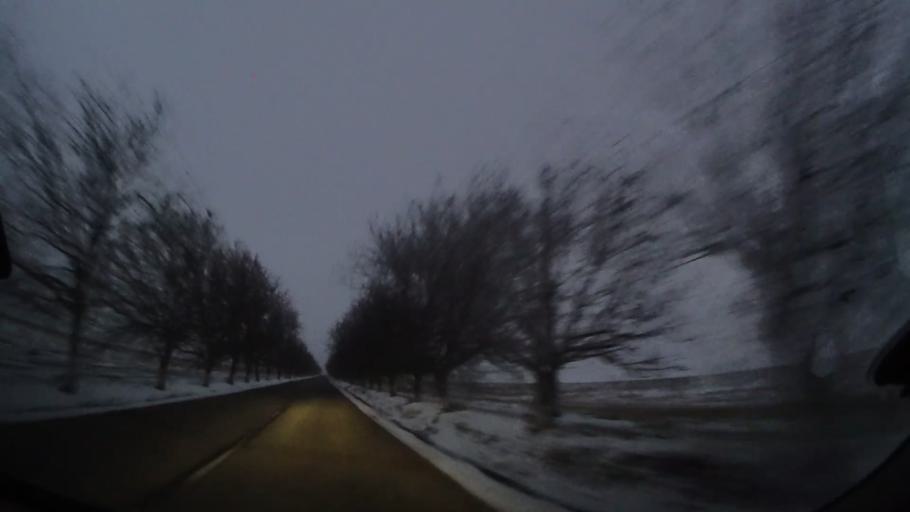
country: RO
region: Vaslui
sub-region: Comuna Dimitrie Cantemir
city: Dimitrie Cantemir
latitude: 46.5184
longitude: 28.0285
